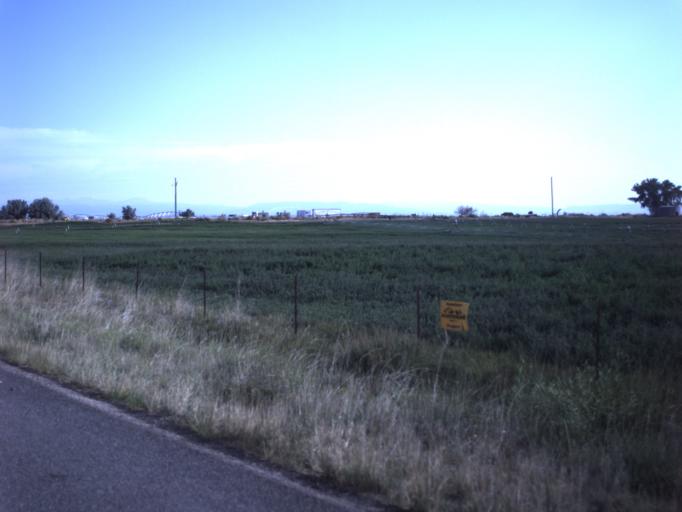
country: US
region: Utah
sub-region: Duchesne County
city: Duchesne
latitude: 40.3032
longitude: -110.2399
